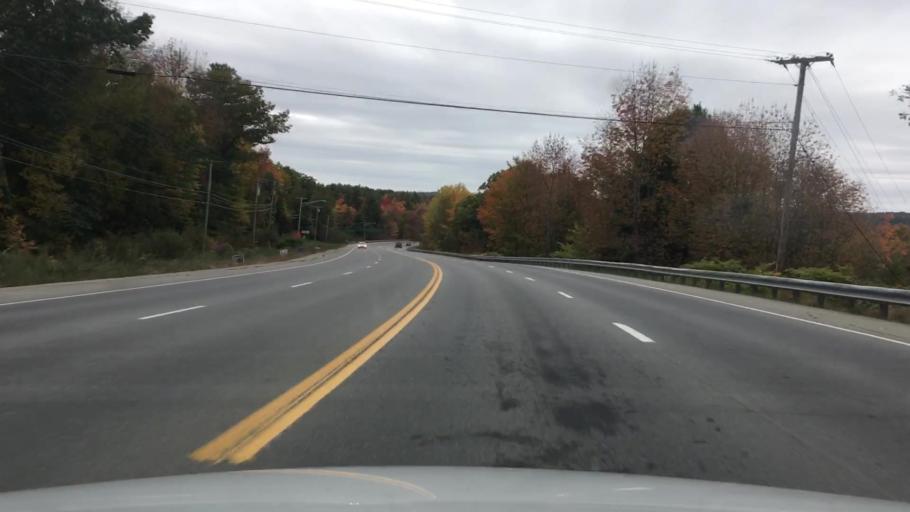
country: US
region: Maine
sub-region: Kennebec County
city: Oakland
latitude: 44.5455
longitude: -69.7004
